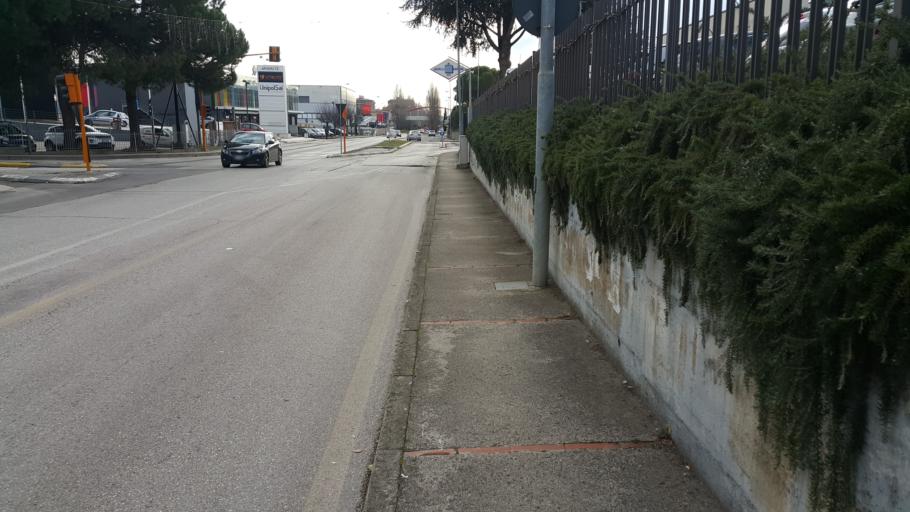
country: IT
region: Umbria
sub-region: Provincia di Perugia
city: Perugia
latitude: 43.0861
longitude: 12.3673
